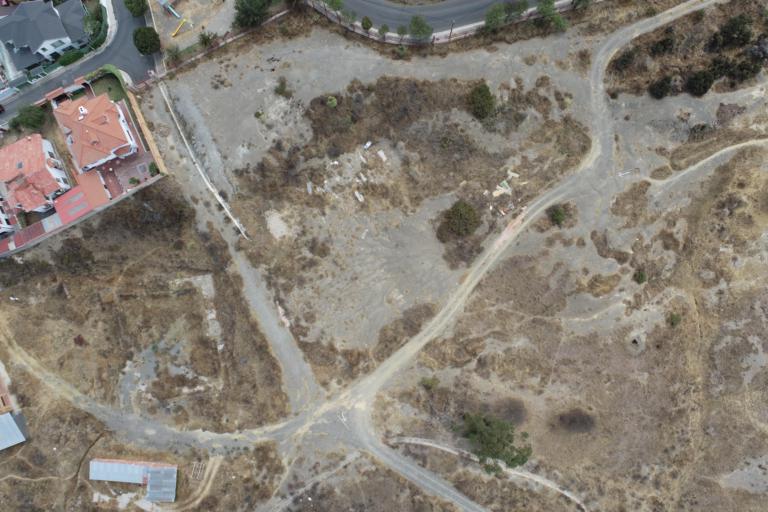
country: BO
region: La Paz
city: La Paz
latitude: -16.5360
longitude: -68.0686
